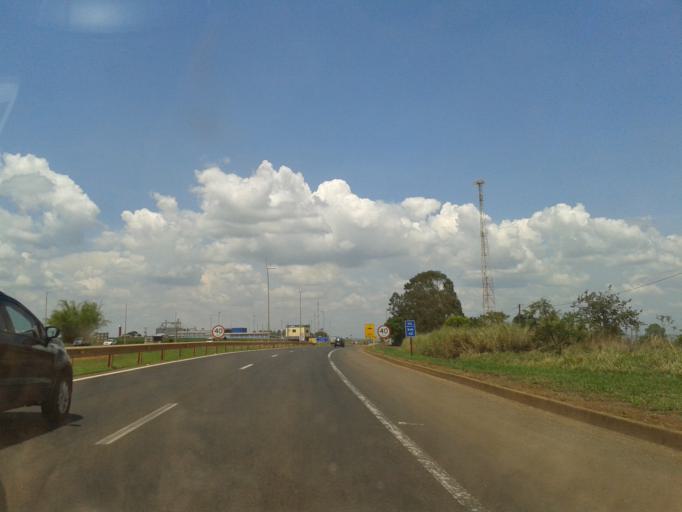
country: BR
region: Minas Gerais
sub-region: Araguari
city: Araguari
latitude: -18.6913
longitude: -48.1804
